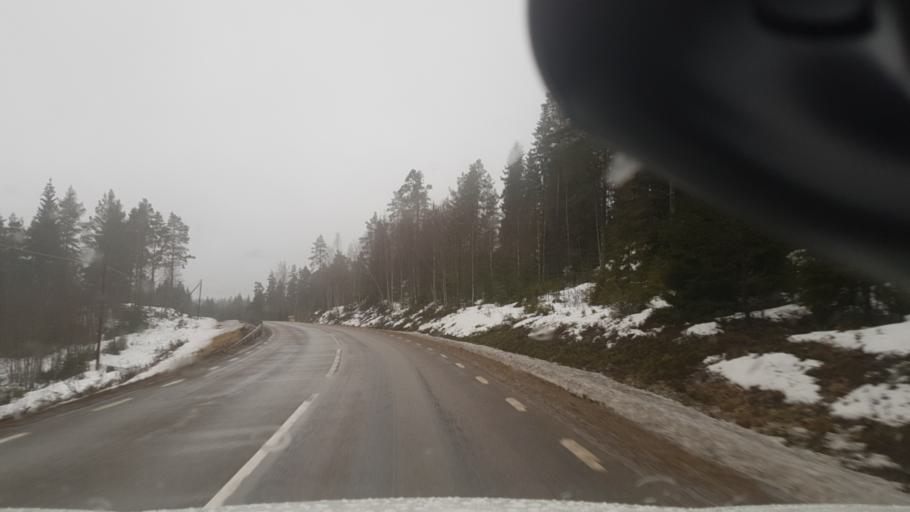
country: SE
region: Vaermland
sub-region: Arjangs Kommun
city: Arjaeng
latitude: 59.5580
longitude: 12.1728
